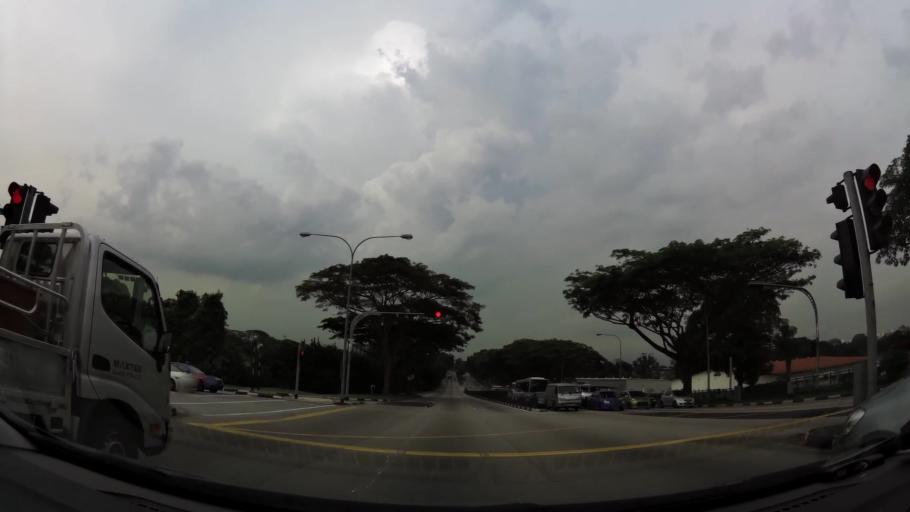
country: MY
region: Johor
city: Kampung Pasir Gudang Baru
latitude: 1.4142
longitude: 103.8232
